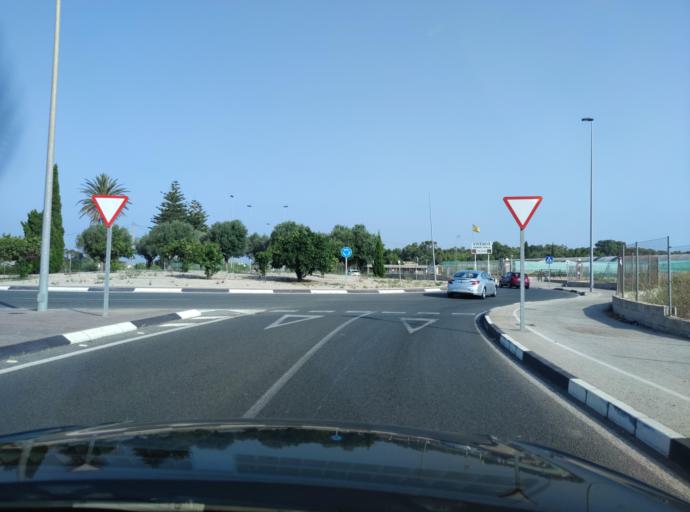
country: ES
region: Valencia
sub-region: Provincia de Alicante
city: Santa Pola
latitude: 38.2051
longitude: -0.5795
